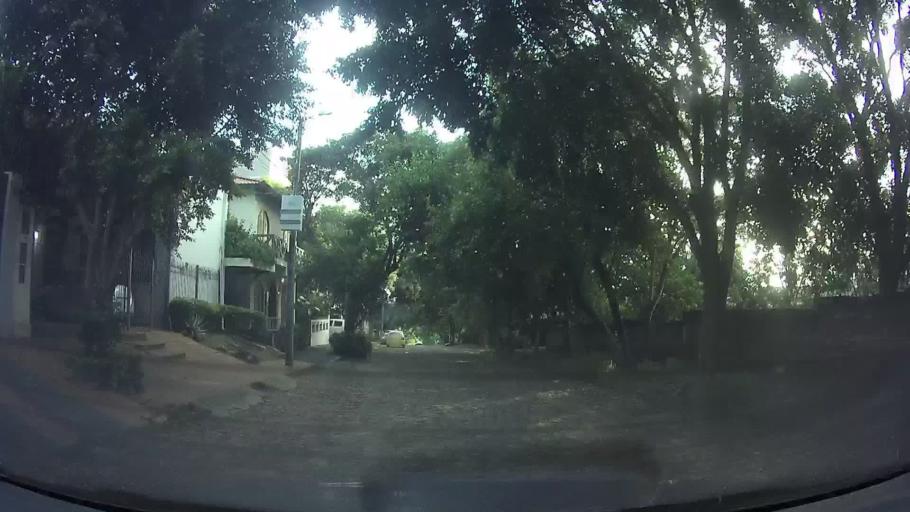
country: PY
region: Asuncion
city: Asuncion
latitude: -25.2672
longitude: -57.5711
